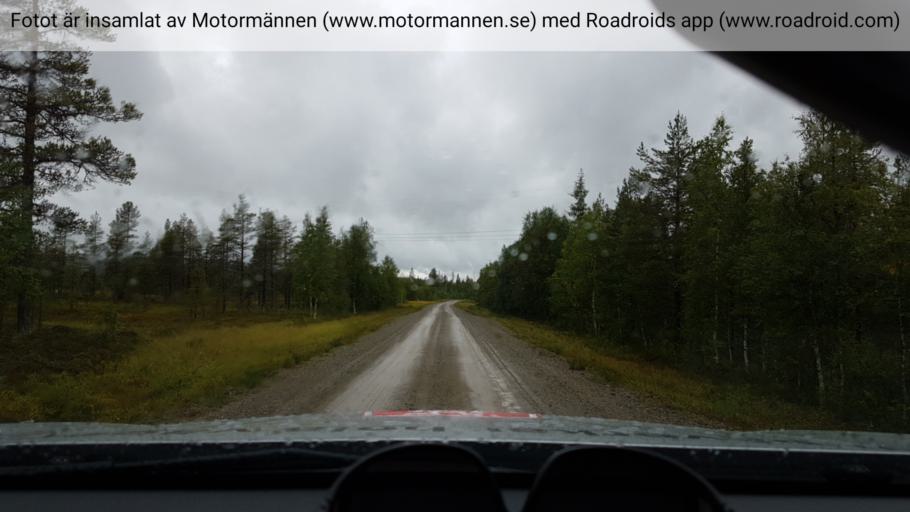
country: SE
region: Vaesterbotten
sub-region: Asele Kommun
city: Insjon
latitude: 64.7848
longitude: 17.5819
